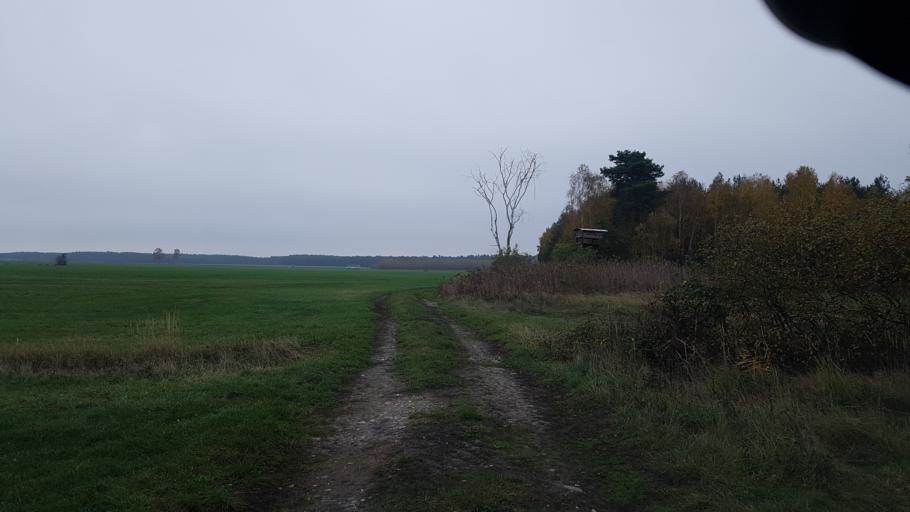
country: DE
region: Brandenburg
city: Ruckersdorf
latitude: 51.5709
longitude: 13.6453
